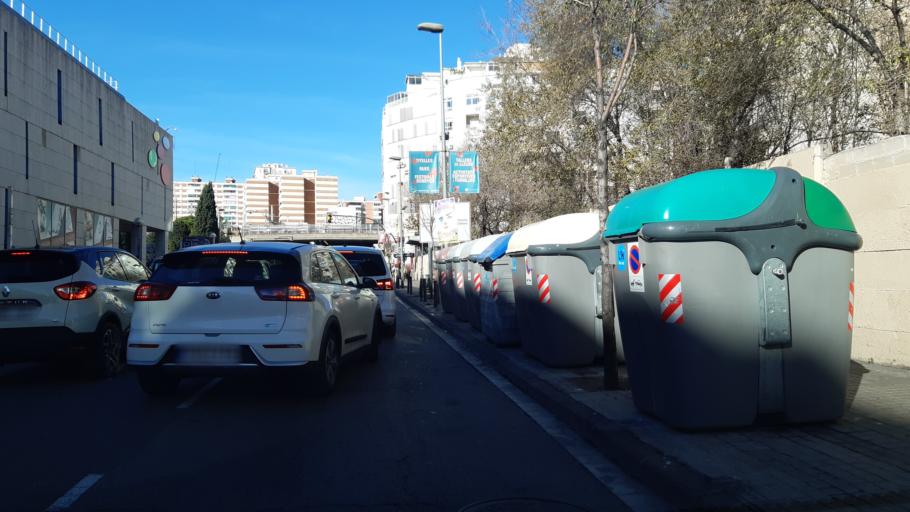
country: ES
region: Catalonia
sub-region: Provincia de Barcelona
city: L'Hospitalet de Llobregat
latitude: 41.3628
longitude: 2.1054
